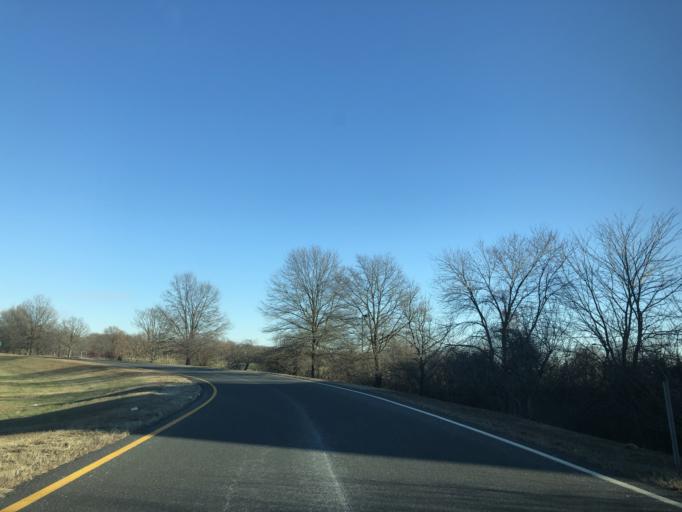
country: US
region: New Jersey
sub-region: Salem County
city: Carneys Point
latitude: 39.7064
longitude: -75.4481
